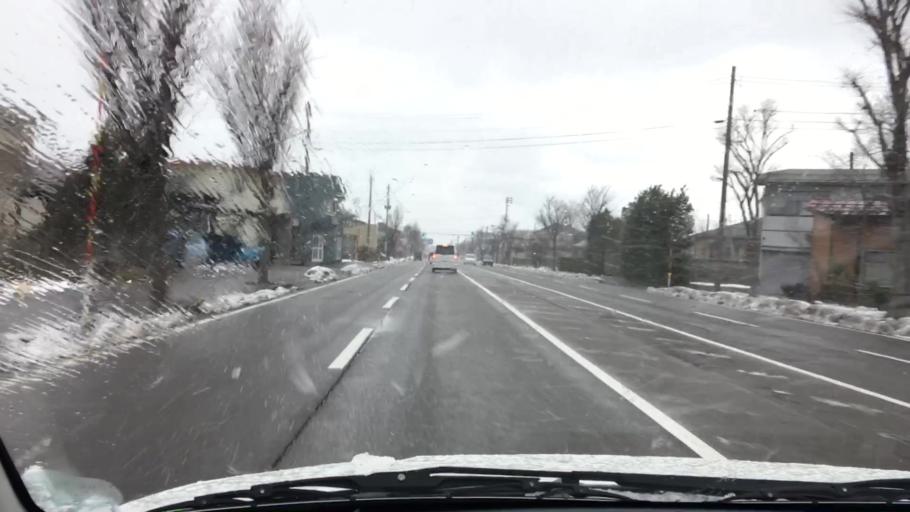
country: JP
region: Niigata
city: Joetsu
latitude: 37.1189
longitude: 138.2327
